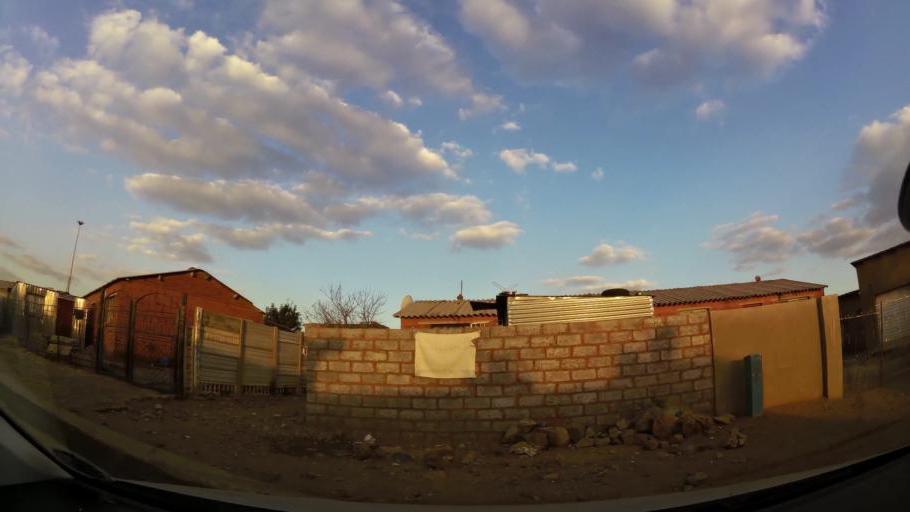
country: ZA
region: Gauteng
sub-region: City of Johannesburg Metropolitan Municipality
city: Soweto
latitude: -26.2728
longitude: 27.8937
